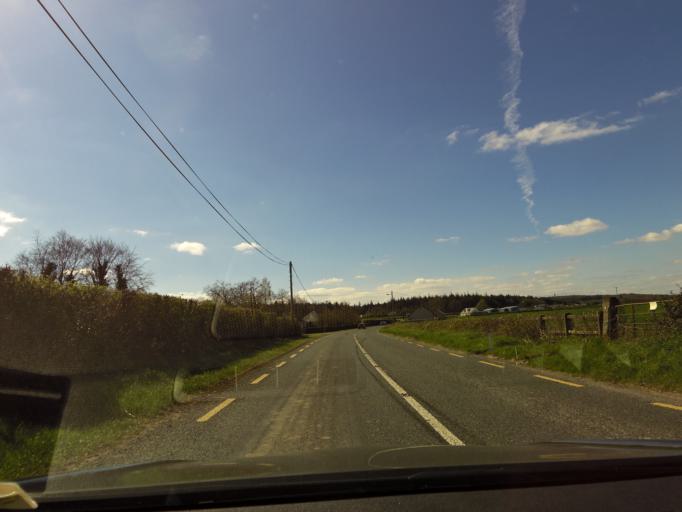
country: IE
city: Ballylinan
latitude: 53.0029
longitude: -7.0671
